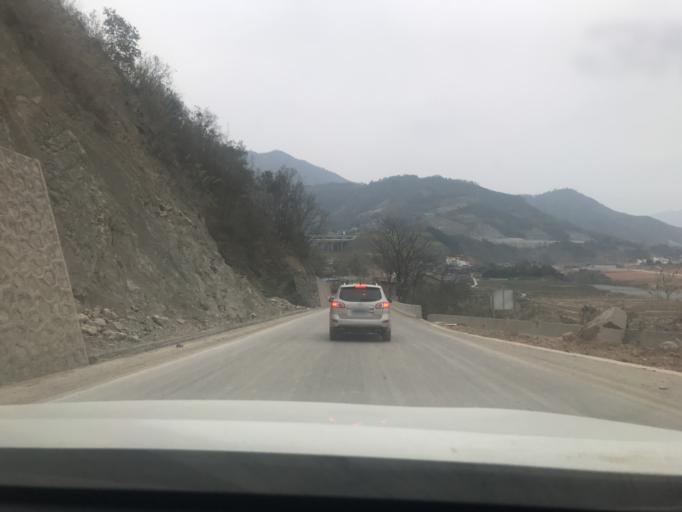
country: CN
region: Guangxi Zhuangzu Zizhiqu
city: Xinzhou
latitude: 25.0174
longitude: 105.8621
